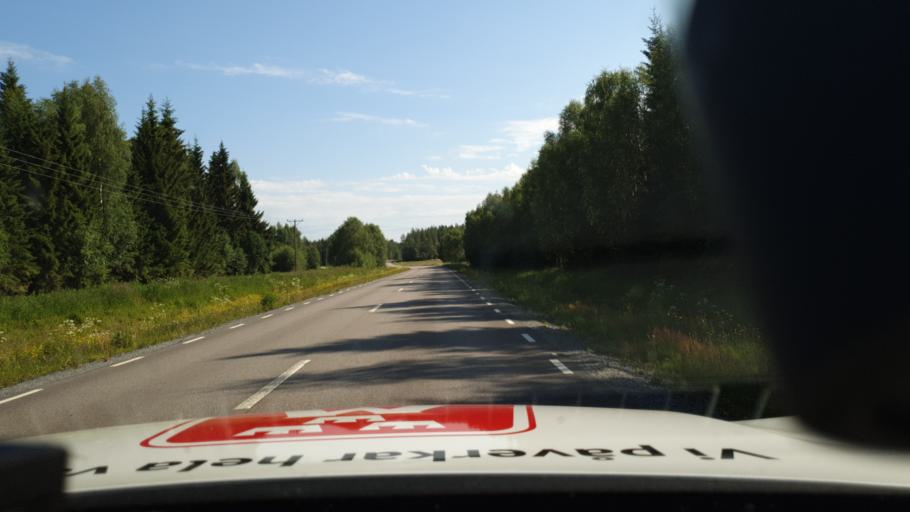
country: SE
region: Norrbotten
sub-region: Lulea Kommun
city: Sodra Sunderbyn
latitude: 65.8251
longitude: 21.9311
